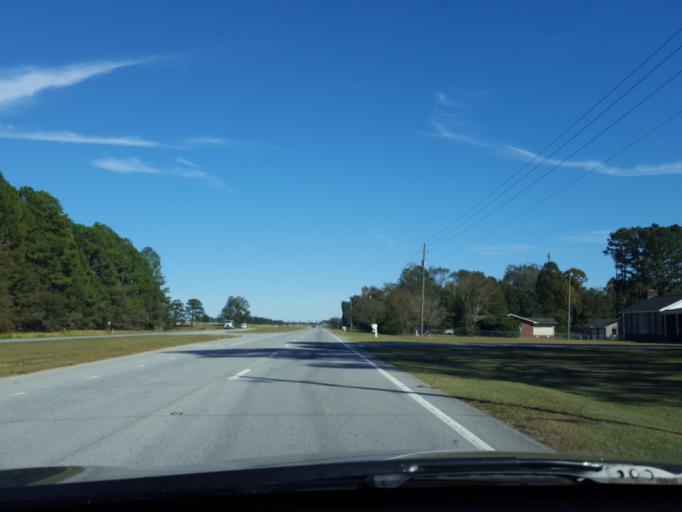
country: US
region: North Carolina
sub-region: Pitt County
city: Greenville
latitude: 35.6256
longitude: -77.2821
